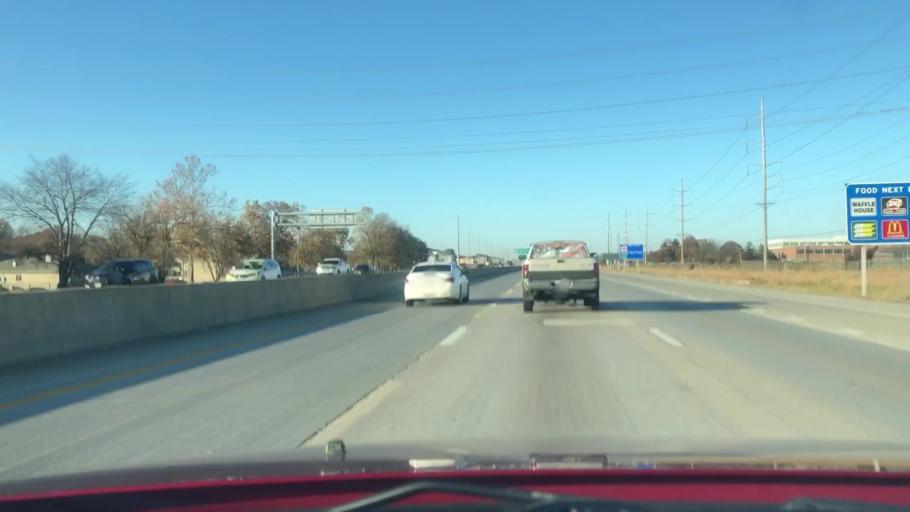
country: US
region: Missouri
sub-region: Greene County
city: Springfield
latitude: 37.1653
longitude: -93.2243
